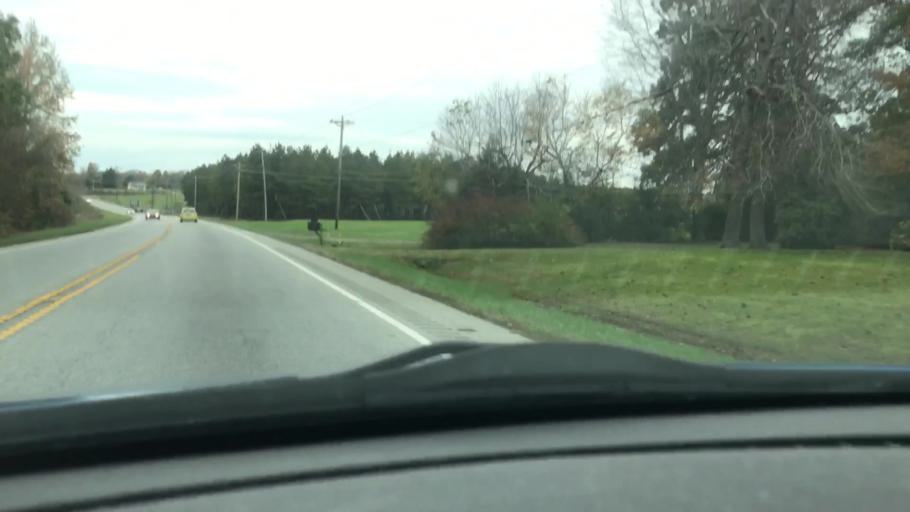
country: US
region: North Carolina
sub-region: Randolph County
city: Trinity
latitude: 35.7501
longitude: -80.0116
